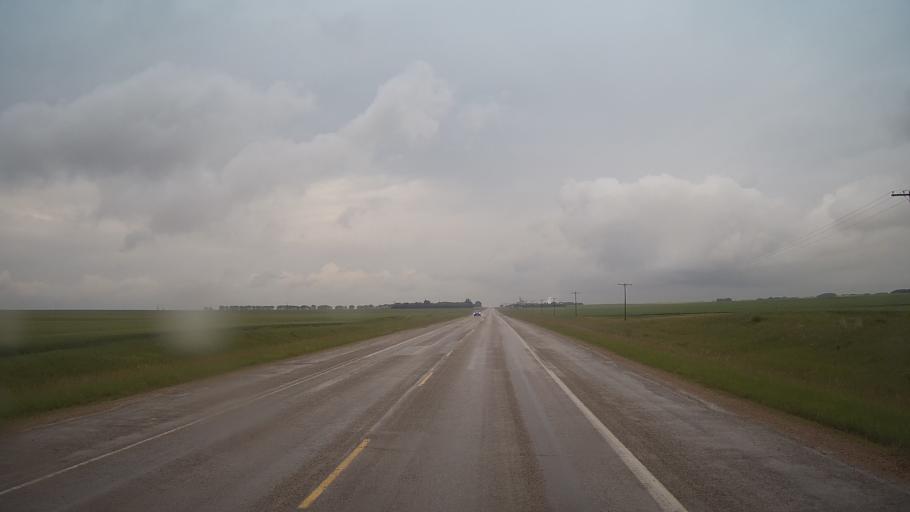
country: CA
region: Saskatchewan
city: Unity
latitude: 52.4350
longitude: -109.0644
